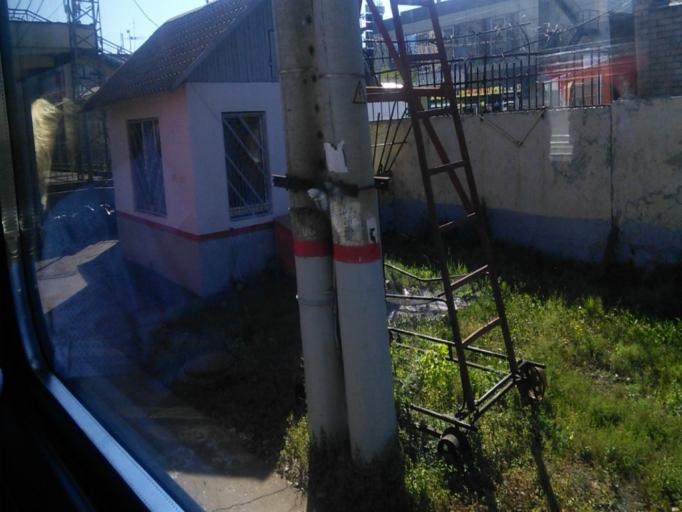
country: RU
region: Moskovskaya
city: Zheleznodorozhnyy
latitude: 55.7522
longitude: 38.0068
